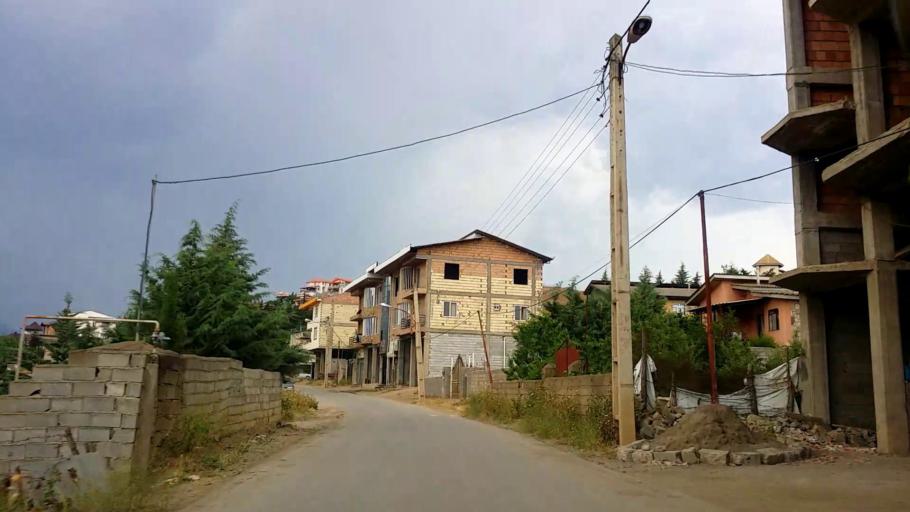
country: IR
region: Mazandaran
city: Chalus
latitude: 36.5149
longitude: 51.2533
